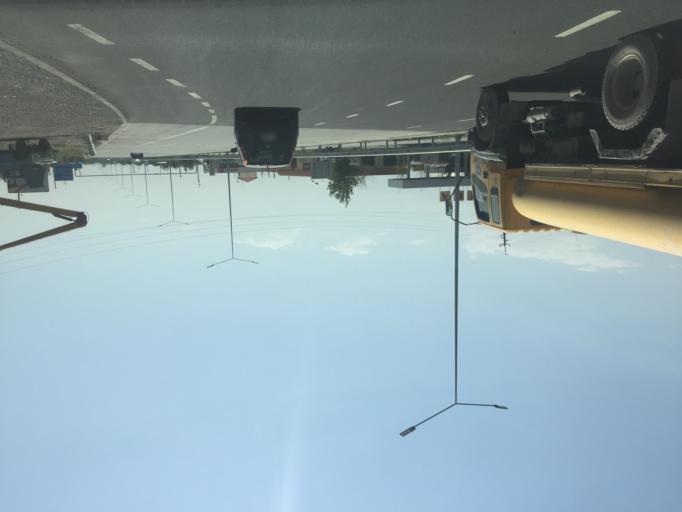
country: AM
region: Ararat
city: Norabats'
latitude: 40.1085
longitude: 44.4716
